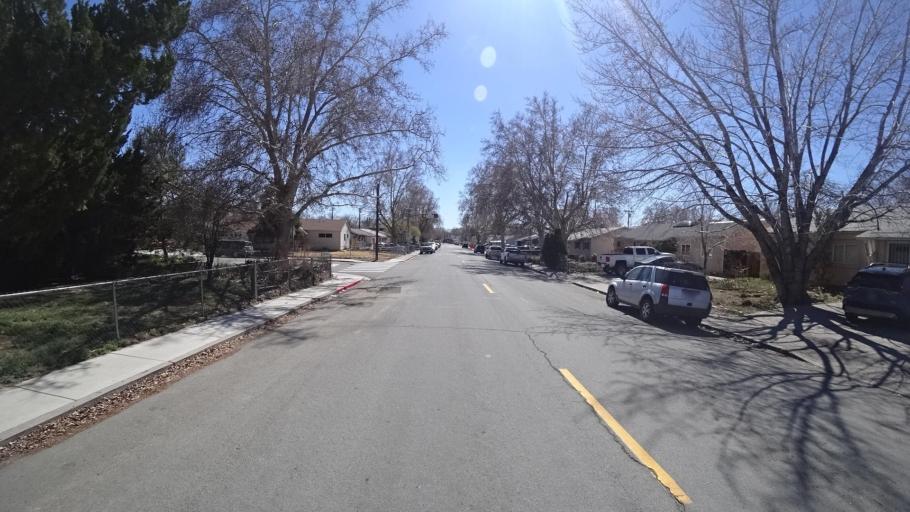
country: US
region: Nevada
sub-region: Washoe County
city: Sparks
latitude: 39.5541
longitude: -119.7485
